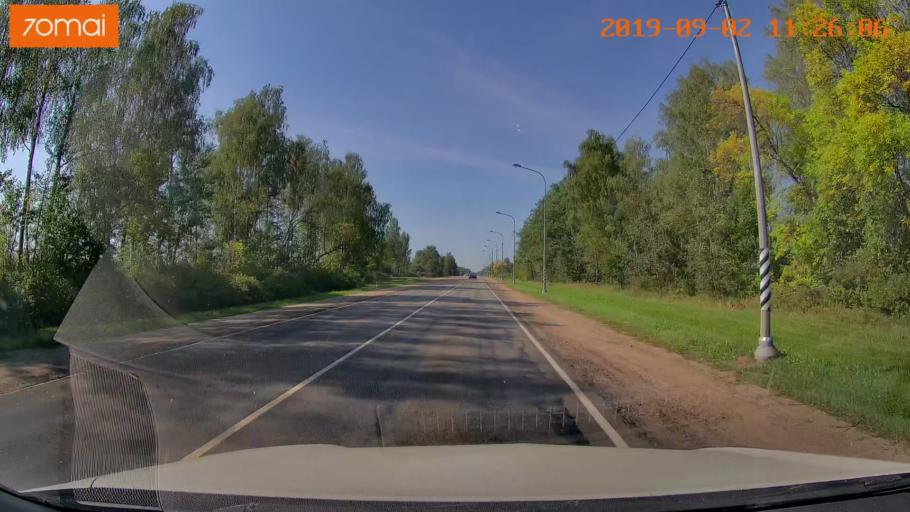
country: RU
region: Smolensk
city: Roslavl'
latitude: 53.9952
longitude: 32.9380
